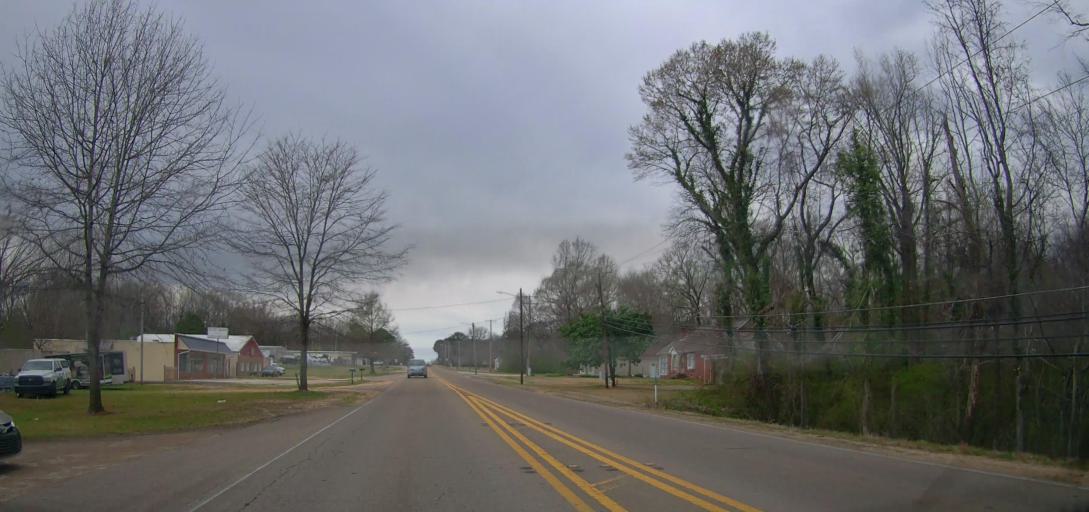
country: US
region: Mississippi
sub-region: Lee County
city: Tupelo
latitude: 34.2578
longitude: -88.6639
